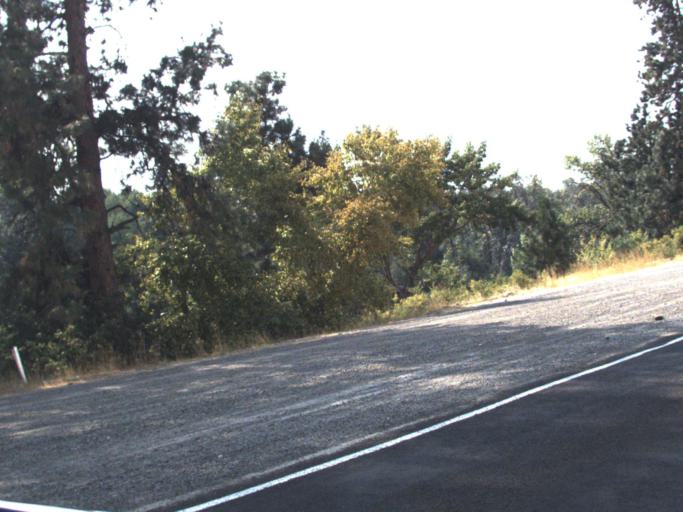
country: US
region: Washington
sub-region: Kittitas County
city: Ellensburg
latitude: 47.1006
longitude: -120.6945
